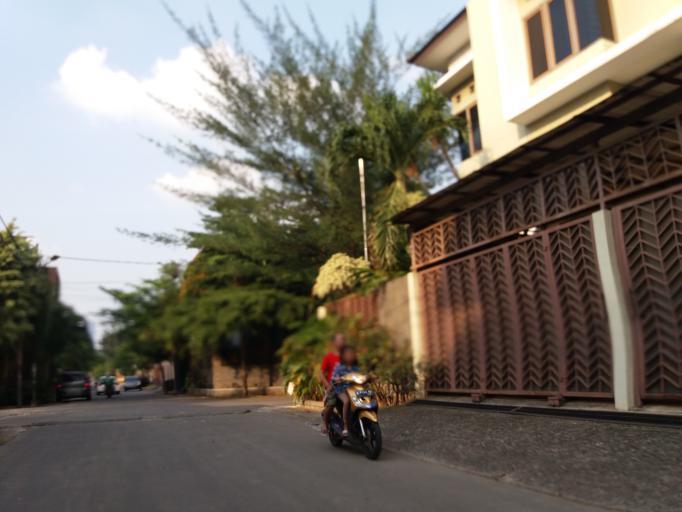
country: ID
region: Jakarta Raya
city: Jakarta
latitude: -6.2470
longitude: 106.8094
